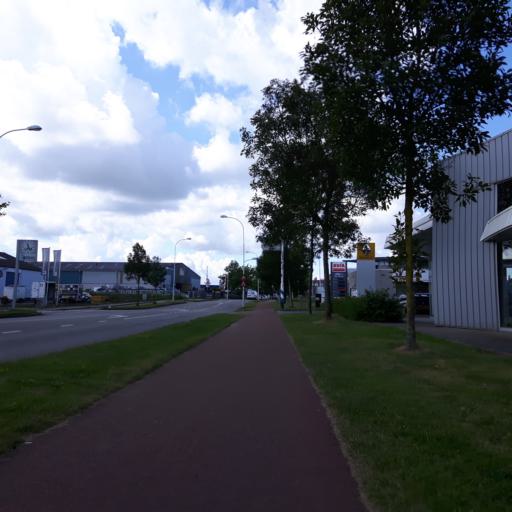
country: NL
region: Zeeland
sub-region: Gemeente Goes
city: Goes
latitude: 51.4936
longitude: 3.8826
